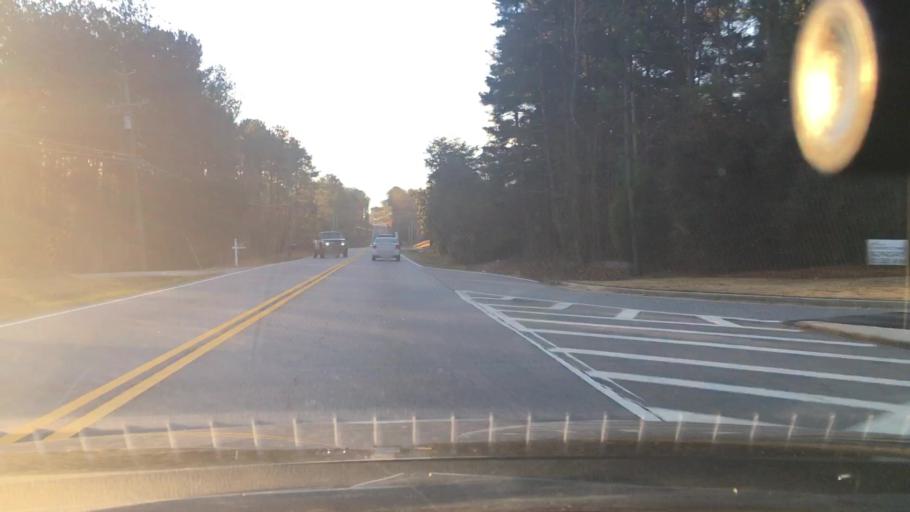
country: US
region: Georgia
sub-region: Fayette County
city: Peachtree City
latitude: 33.3999
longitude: -84.6808
